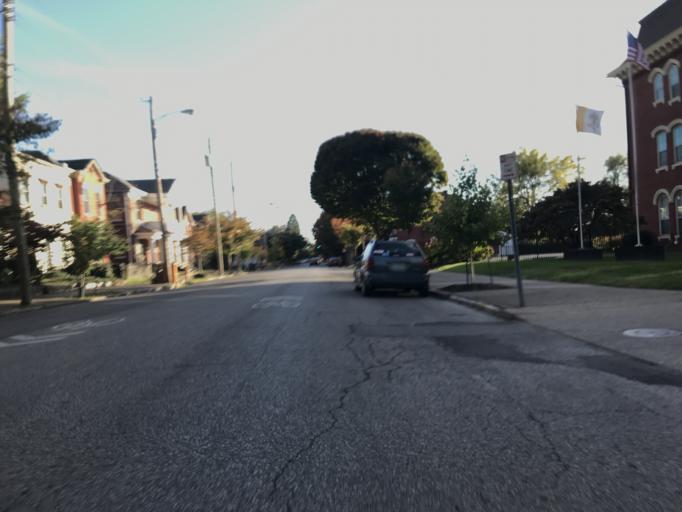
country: US
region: Kentucky
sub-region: Jefferson County
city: Louisville
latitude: 38.2368
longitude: -85.7635
